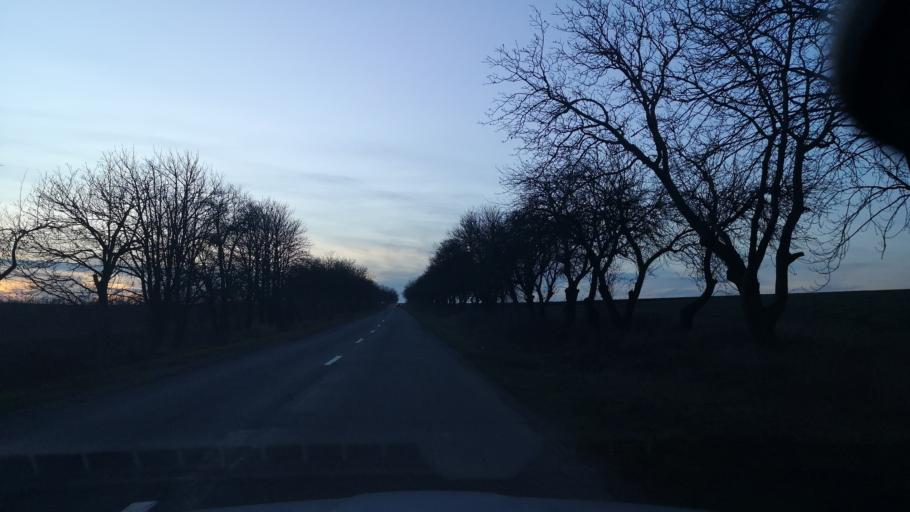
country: MD
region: Orhei
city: Orhei
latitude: 47.3121
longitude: 28.9565
